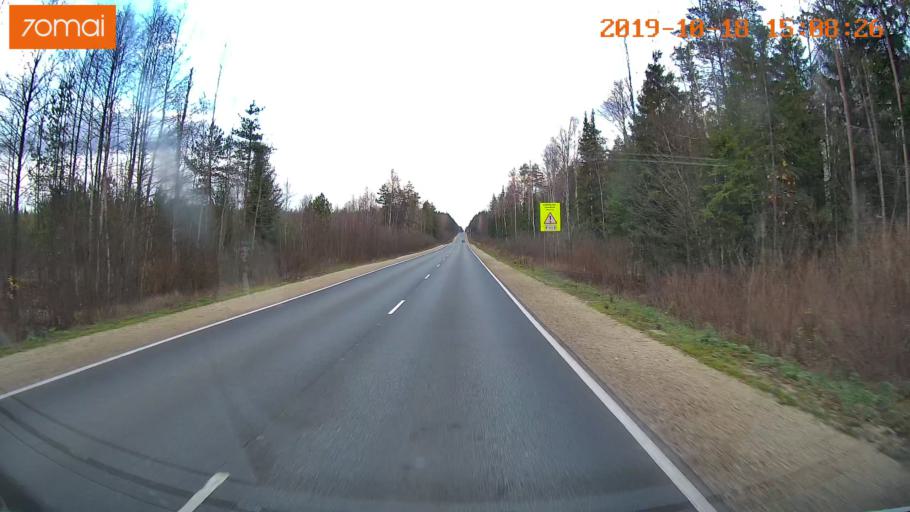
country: RU
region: Vladimir
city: Gus'-Khrustal'nyy
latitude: 55.5524
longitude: 40.6106
